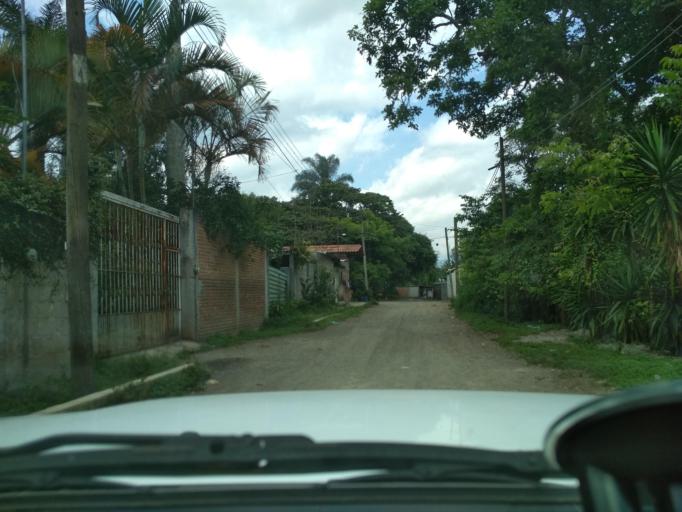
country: MX
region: Veracruz
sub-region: Fortin
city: Monte Salas
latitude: 18.9360
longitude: -97.0166
